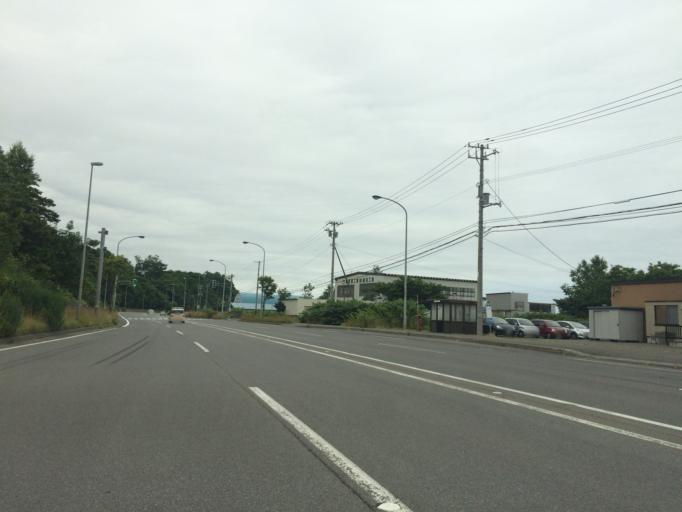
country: JP
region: Hokkaido
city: Otaru
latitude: 43.1357
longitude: 141.1737
